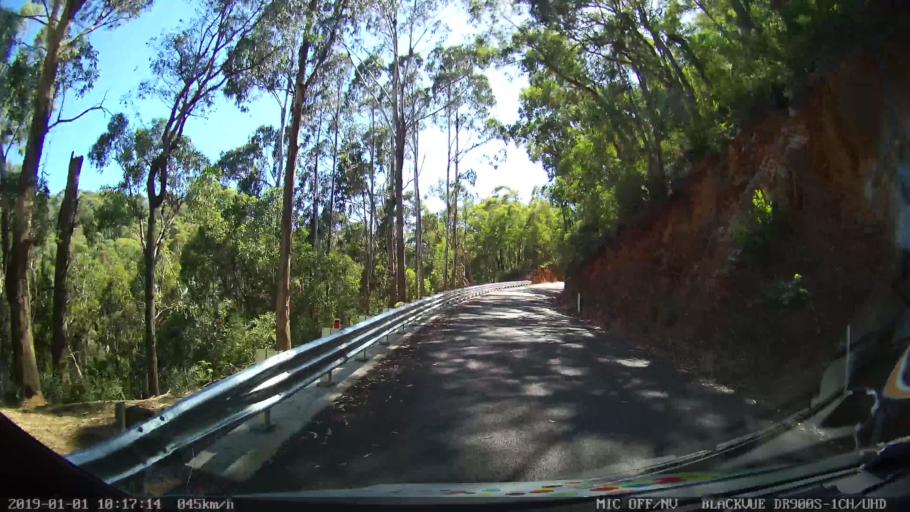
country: AU
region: New South Wales
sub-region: Snowy River
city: Jindabyne
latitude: -36.0911
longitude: 148.1743
